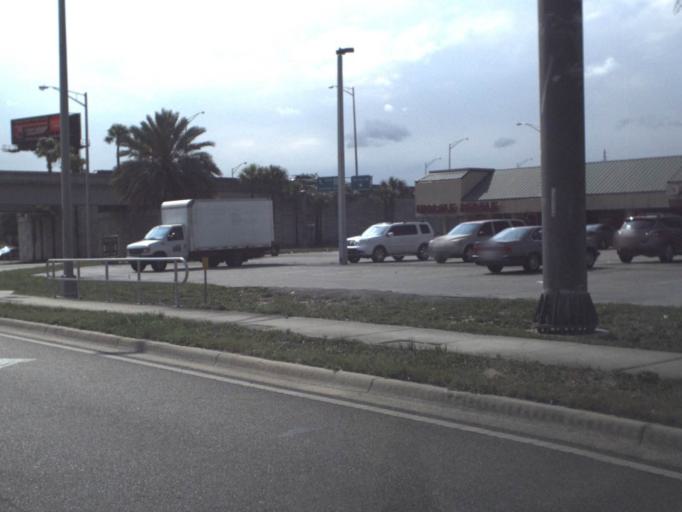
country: US
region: Florida
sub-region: Duval County
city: Jacksonville
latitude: 30.2868
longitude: -81.5580
